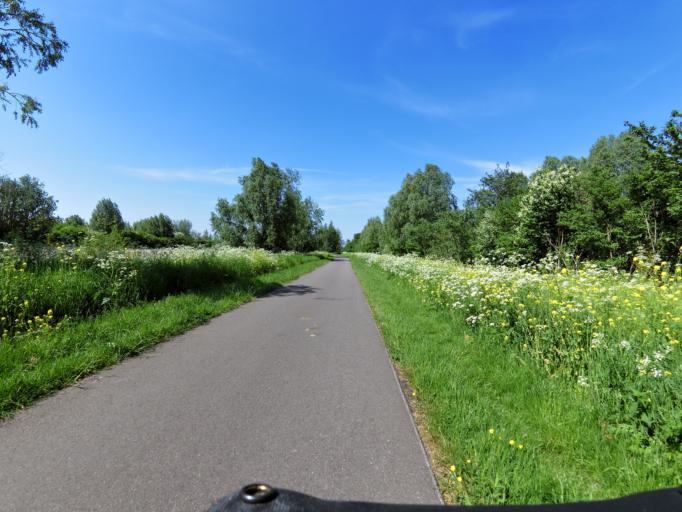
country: NL
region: South Holland
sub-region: Gemeente Barendrecht
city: Barendrecht
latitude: 51.8346
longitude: 4.5189
